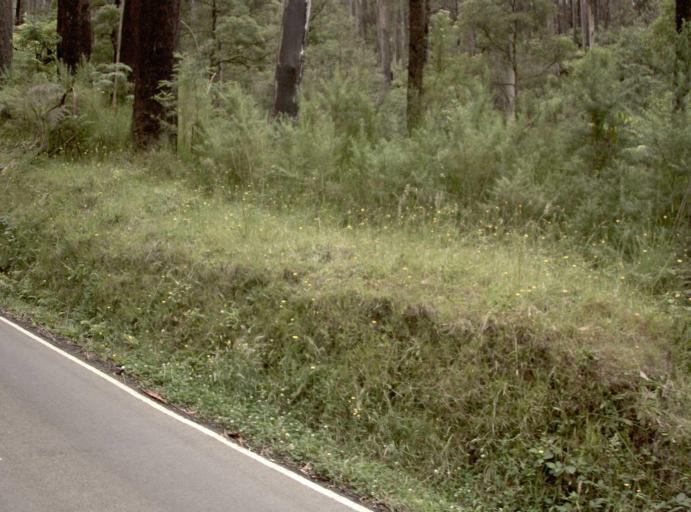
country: AU
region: Victoria
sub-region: Yarra Ranges
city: Healesville
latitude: -37.5915
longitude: 145.6393
